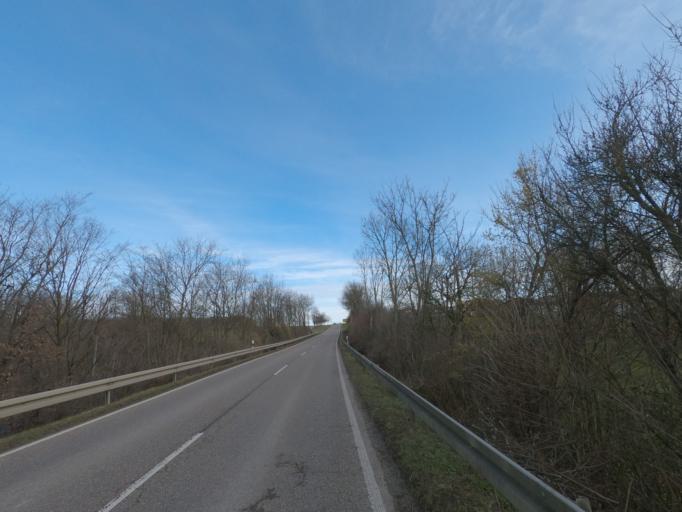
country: DE
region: Baden-Wuerttemberg
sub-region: Regierungsbezirk Stuttgart
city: Zell unter Aichelberg
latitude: 48.6496
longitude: 9.5653
